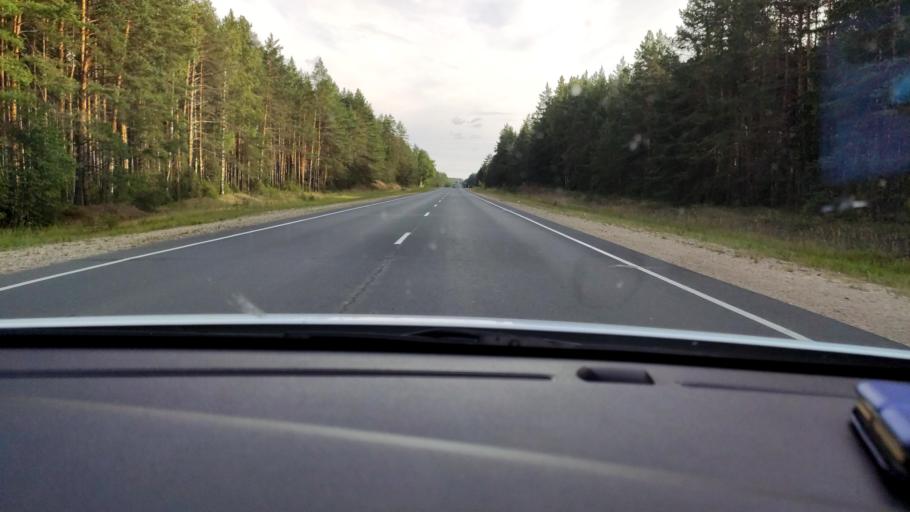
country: RU
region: Mariy-El
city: Suslonger
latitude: 56.3286
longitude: 48.2352
